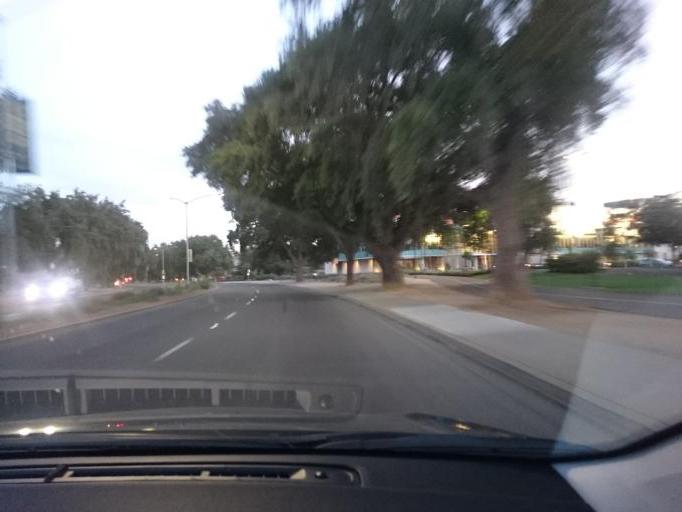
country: US
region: California
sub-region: Yolo County
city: Davis
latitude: 38.5435
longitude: -121.7605
